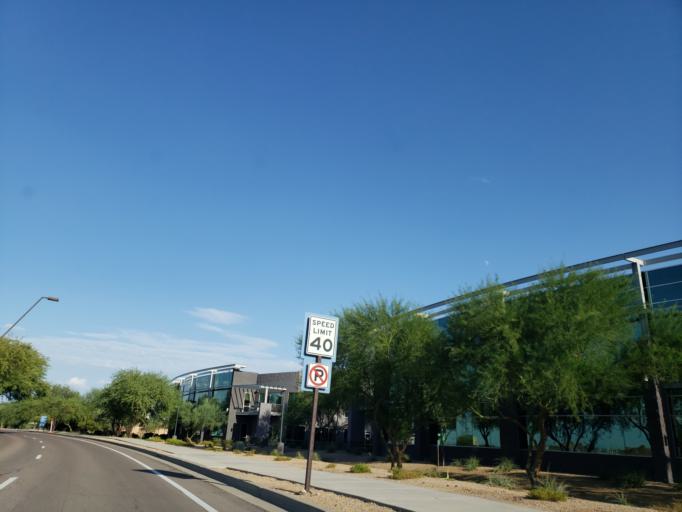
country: US
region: Arizona
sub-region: Maricopa County
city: Tempe Junction
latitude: 33.4305
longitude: -111.9554
